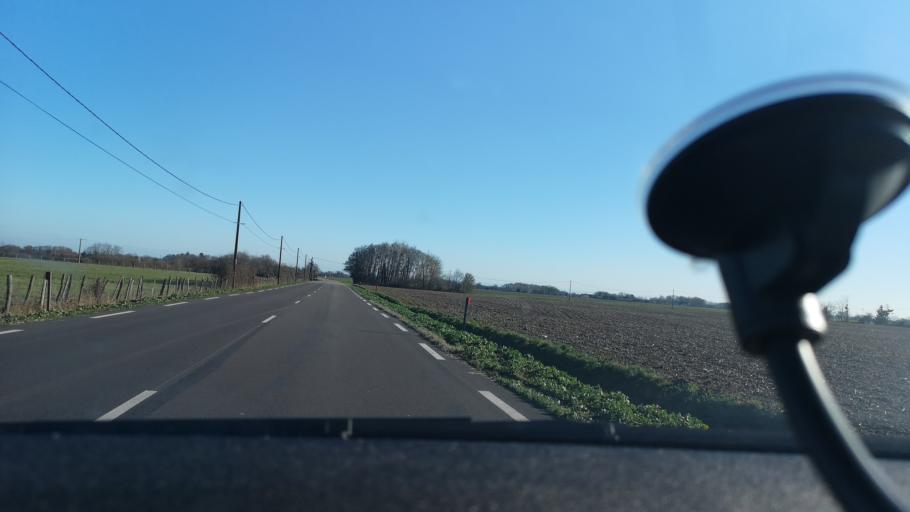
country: FR
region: Bourgogne
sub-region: Departement de Saone-et-Loire
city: Saint-Martin-en-Bresse
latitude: 46.7443
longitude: 5.0660
